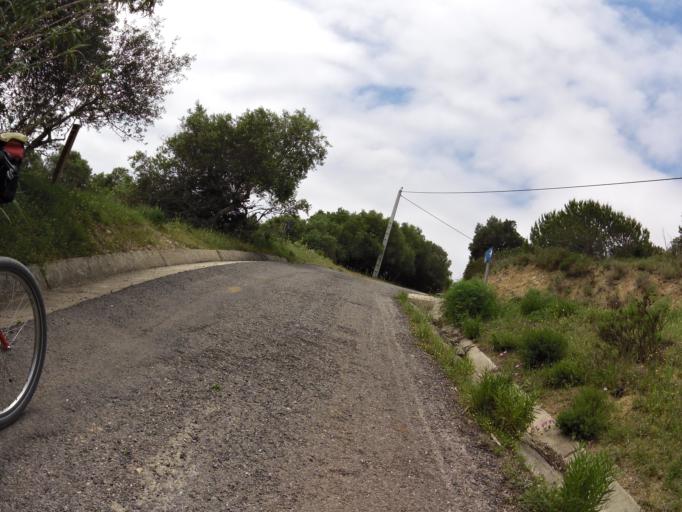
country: PT
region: Faro
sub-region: Vila do Bispo
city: Vila do Bispo
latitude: 37.0736
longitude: -8.8750
